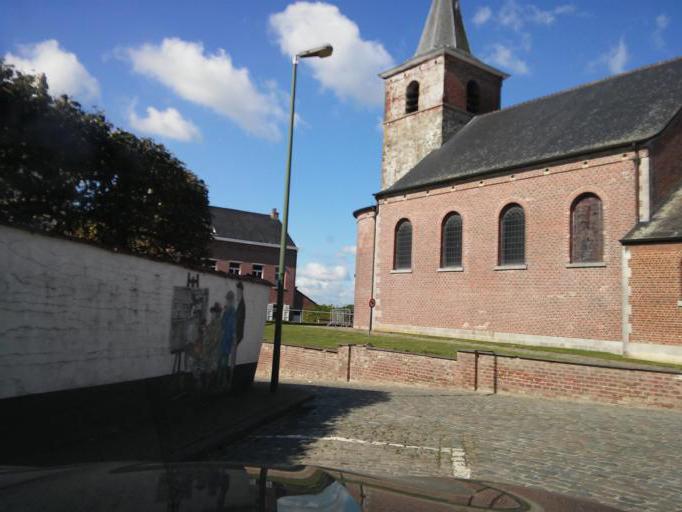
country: BE
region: Flanders
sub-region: Provincie Vlaams-Brabant
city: Pepingen
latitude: 50.7396
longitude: 4.1353
